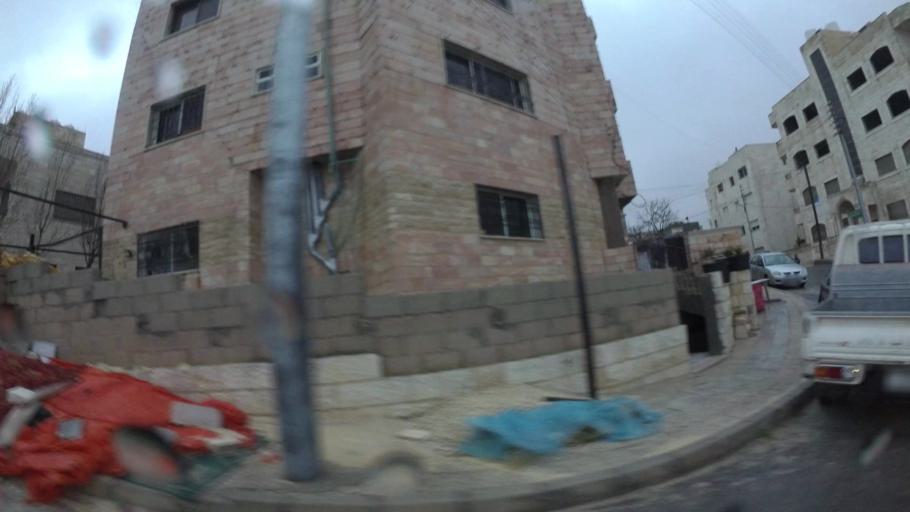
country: JO
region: Amman
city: Al Jubayhah
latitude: 32.0285
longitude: 35.8447
